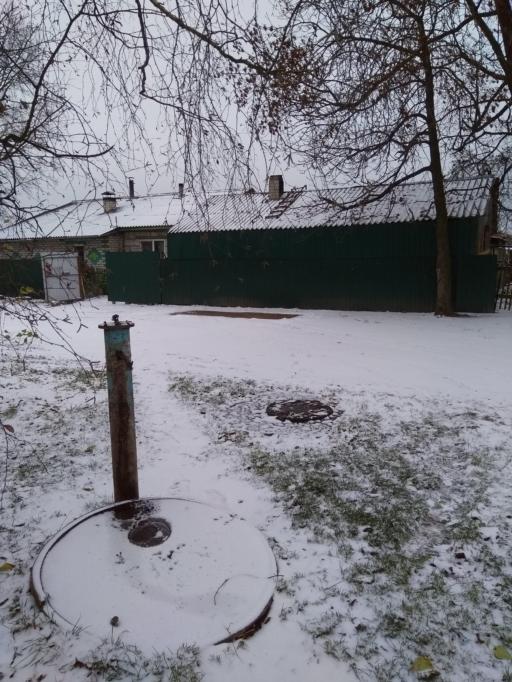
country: BY
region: Mogilev
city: Palykavichy Pyershyya
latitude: 54.0337
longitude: 30.3267
